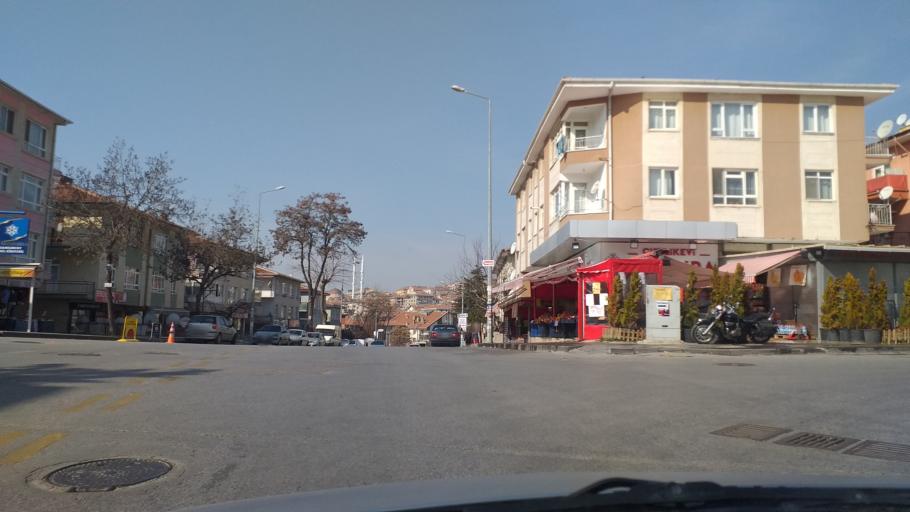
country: TR
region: Ankara
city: Ankara
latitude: 39.9846
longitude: 32.8535
